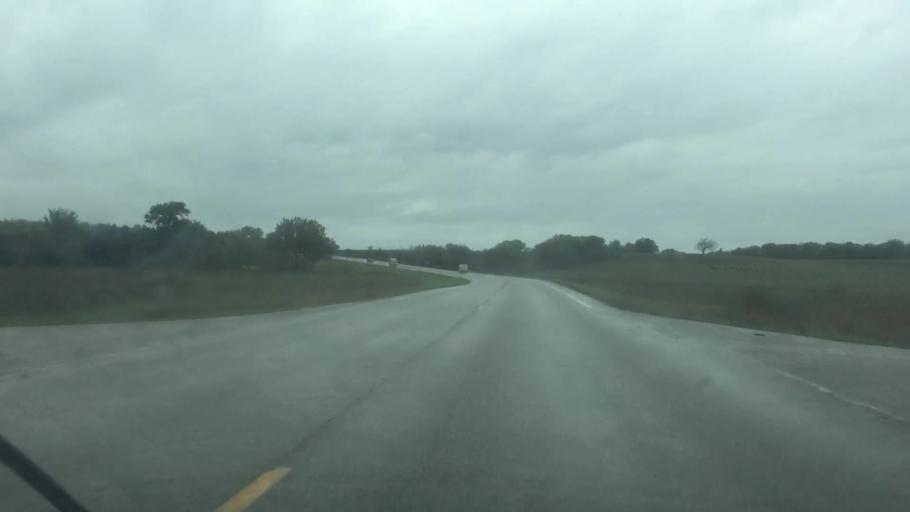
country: US
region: Kansas
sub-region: Anderson County
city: Garnett
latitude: 38.3911
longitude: -95.1027
